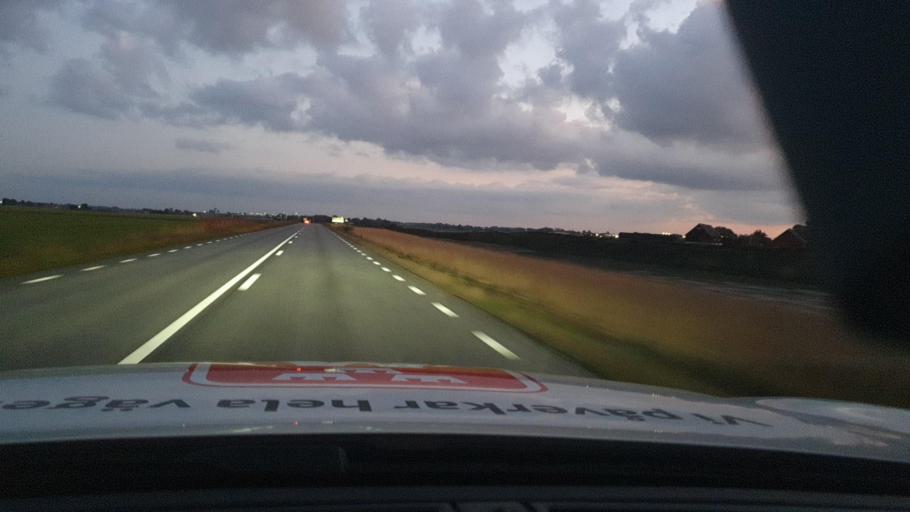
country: SE
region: Skane
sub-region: Angelholms Kommun
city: AEngelholm
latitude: 56.2964
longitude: 12.8739
